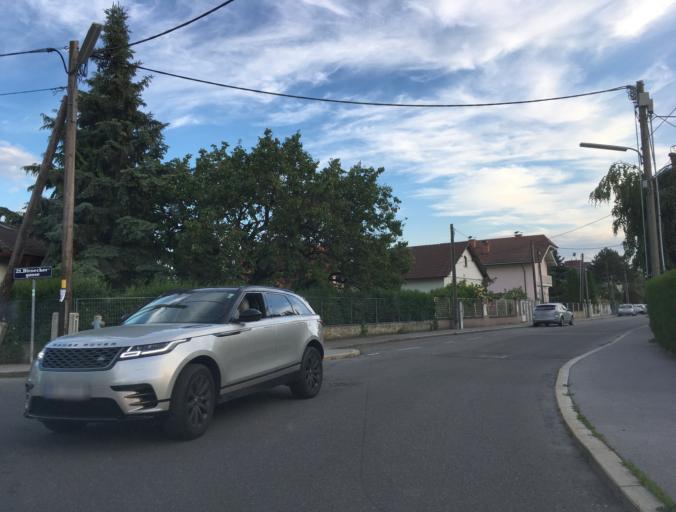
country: AT
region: Vienna
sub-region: Wien Stadt
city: Vienna
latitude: 48.2448
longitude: 16.4006
